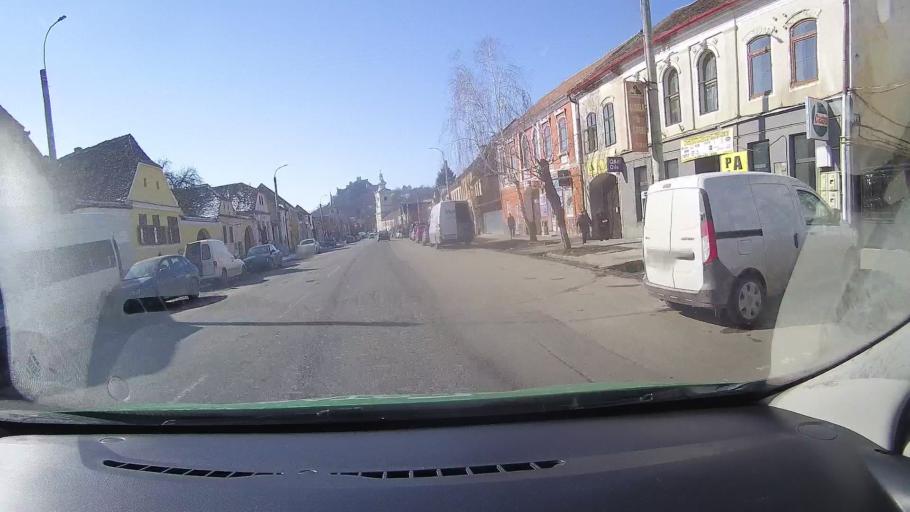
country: RO
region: Brasov
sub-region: Oras Rupea
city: Rupea
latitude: 46.0395
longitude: 25.2256
